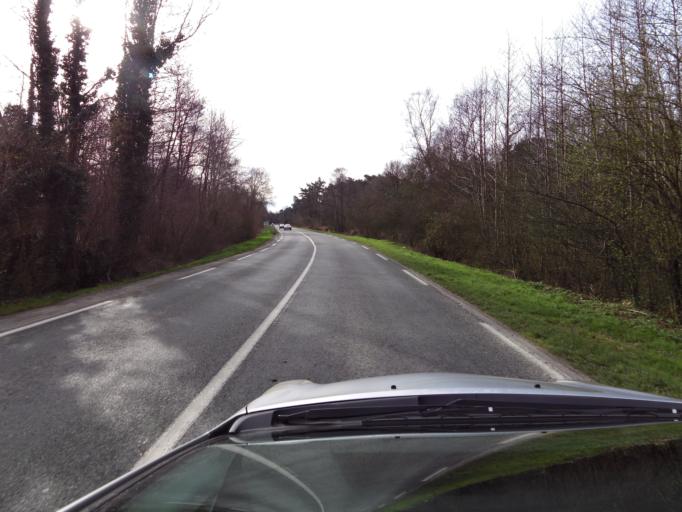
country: FR
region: Picardie
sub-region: Departement de l'Oise
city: Ver-sur-Launette
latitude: 49.1419
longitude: 2.6836
